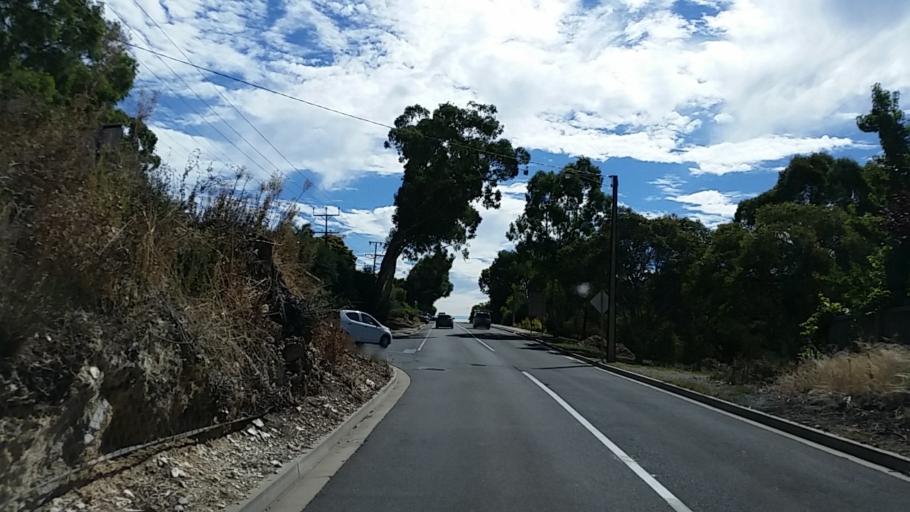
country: AU
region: South Australia
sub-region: Campbelltown
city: Athelstone
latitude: -34.8639
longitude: 138.7150
